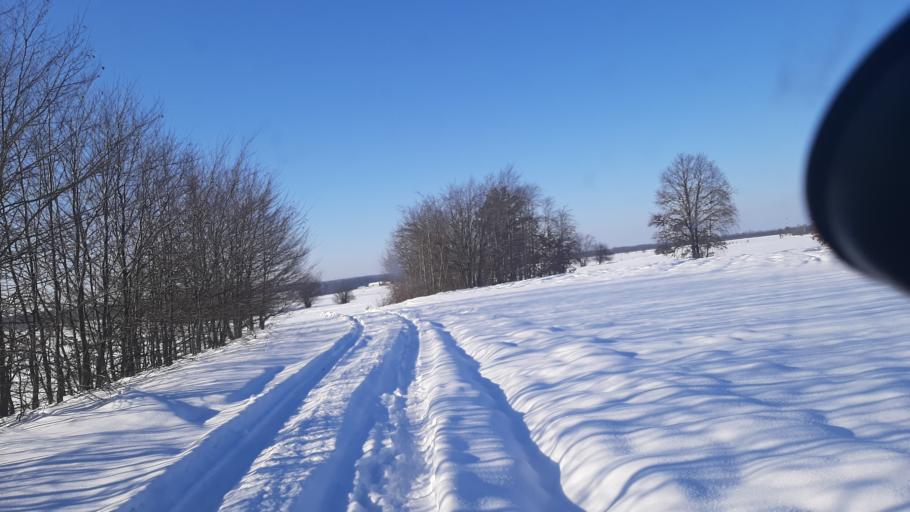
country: PL
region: Lublin Voivodeship
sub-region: Powiat lubelski
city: Jastkow
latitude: 51.3783
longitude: 22.4343
